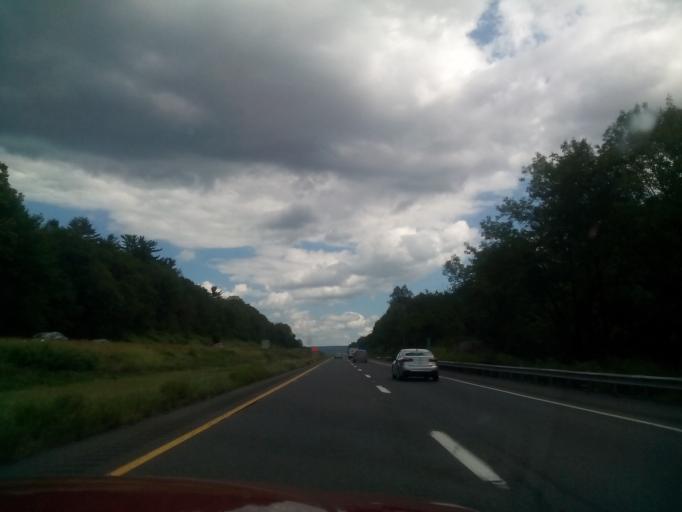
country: US
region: Pennsylvania
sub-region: Monroe County
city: Arlington Heights
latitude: 40.9928
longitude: -75.2546
